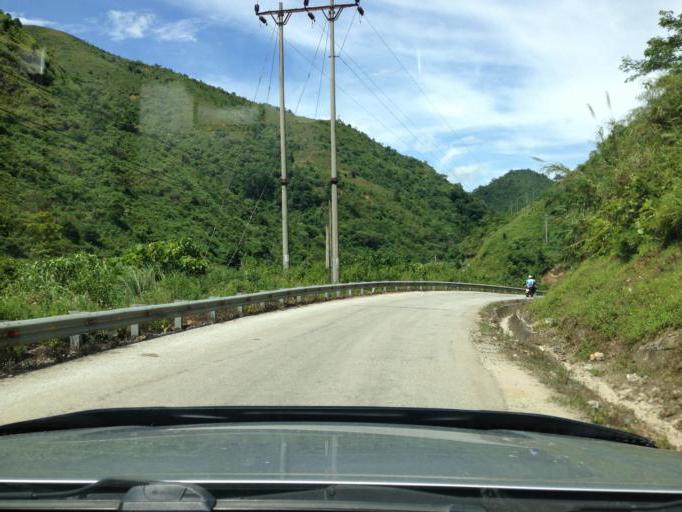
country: VN
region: Lao Cai
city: Thi Tran Khanh Yen
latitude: 22.0315
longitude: 104.0810
